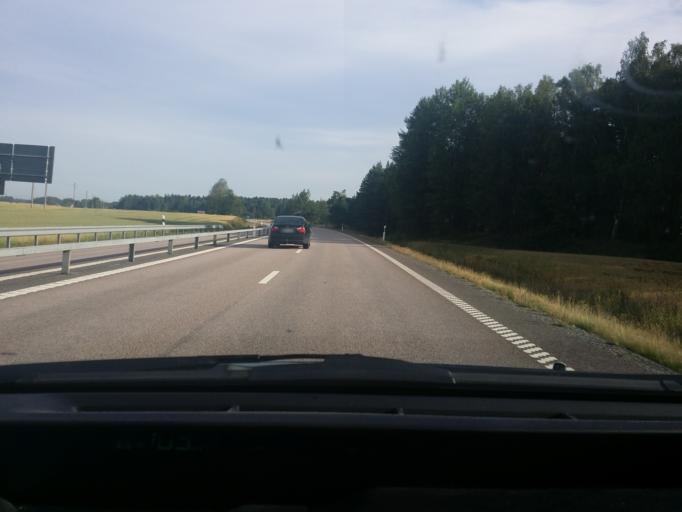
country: SE
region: Vaestmanland
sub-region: Vasteras
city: Tillberga
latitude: 59.7122
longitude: 16.5835
